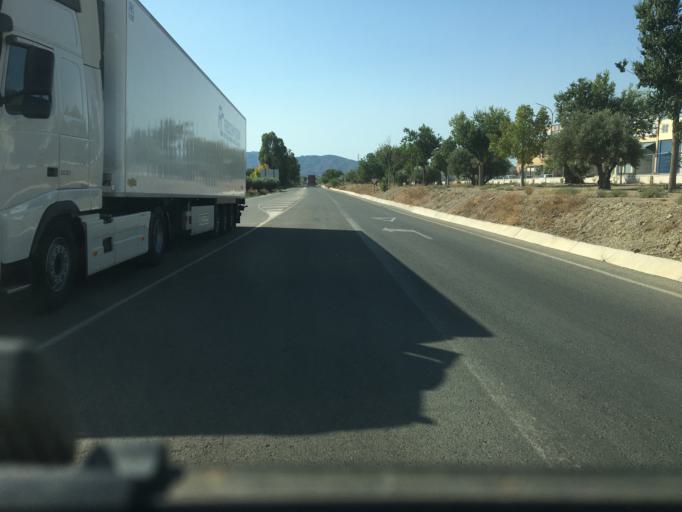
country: ES
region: Andalusia
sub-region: Provincia de Almeria
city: Huercal-Overa
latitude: 37.4154
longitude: -1.9657
